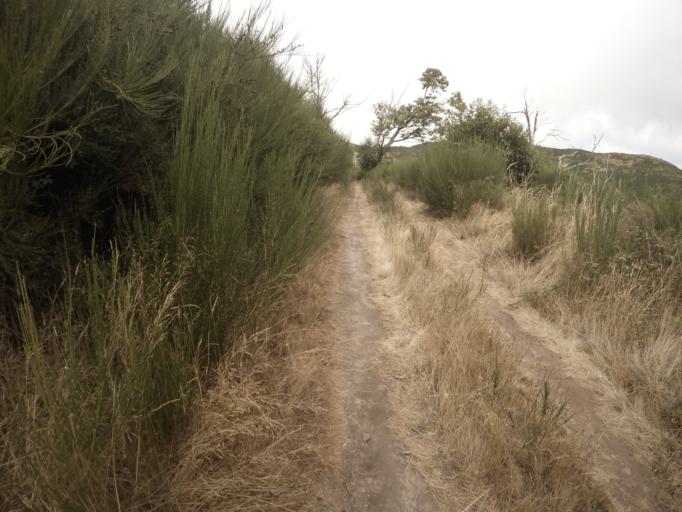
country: PT
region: Madeira
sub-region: Camara de Lobos
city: Curral das Freiras
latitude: 32.7099
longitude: -16.9973
